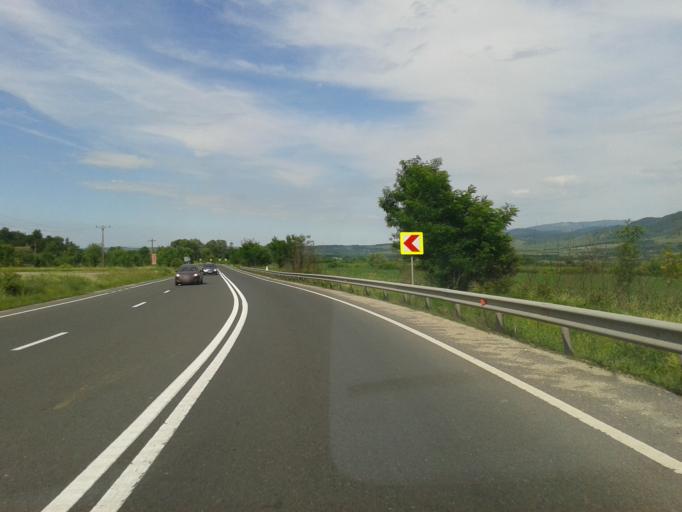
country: RO
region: Hunedoara
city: Berca
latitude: 45.6256
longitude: 22.9905
